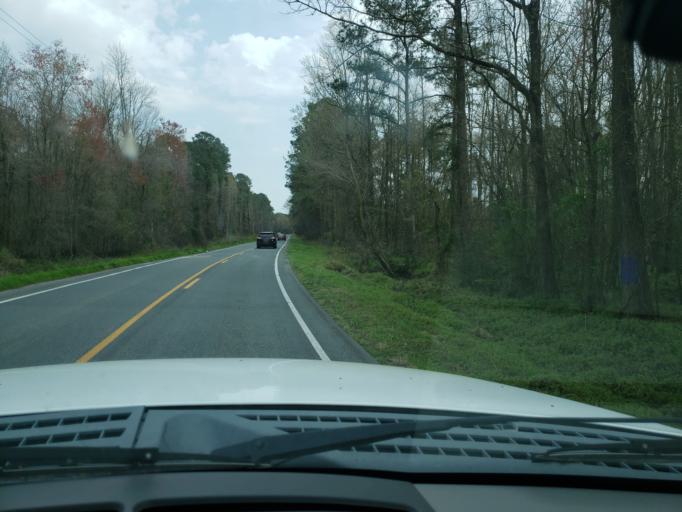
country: US
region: North Carolina
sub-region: Duplin County
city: Beulaville
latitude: 34.7898
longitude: -77.8451
